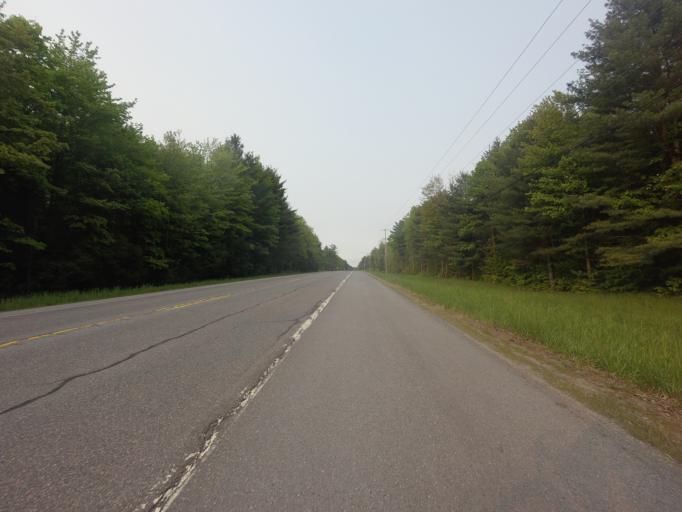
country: US
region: New York
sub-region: Jefferson County
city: Carthage
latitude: 44.0928
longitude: -75.4215
